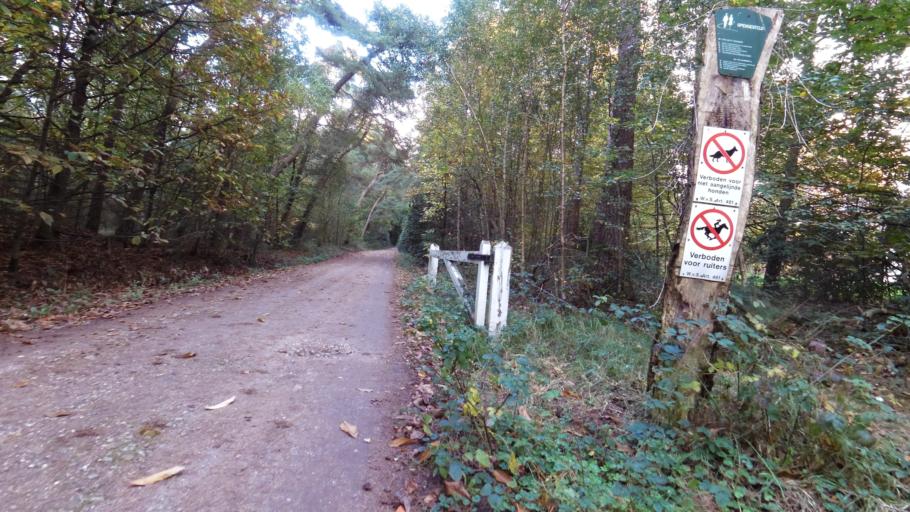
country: NL
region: Gelderland
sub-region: Gemeente Ede
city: Wekerom
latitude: 52.0840
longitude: 5.6975
